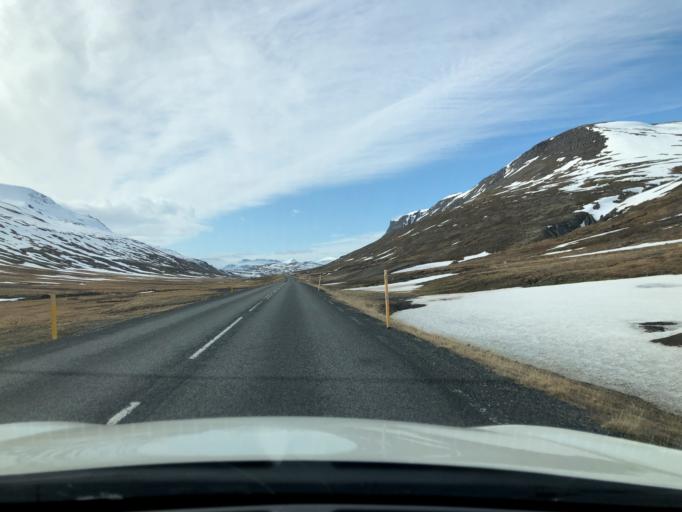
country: IS
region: East
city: Egilsstadir
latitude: 65.1340
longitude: -14.3361
